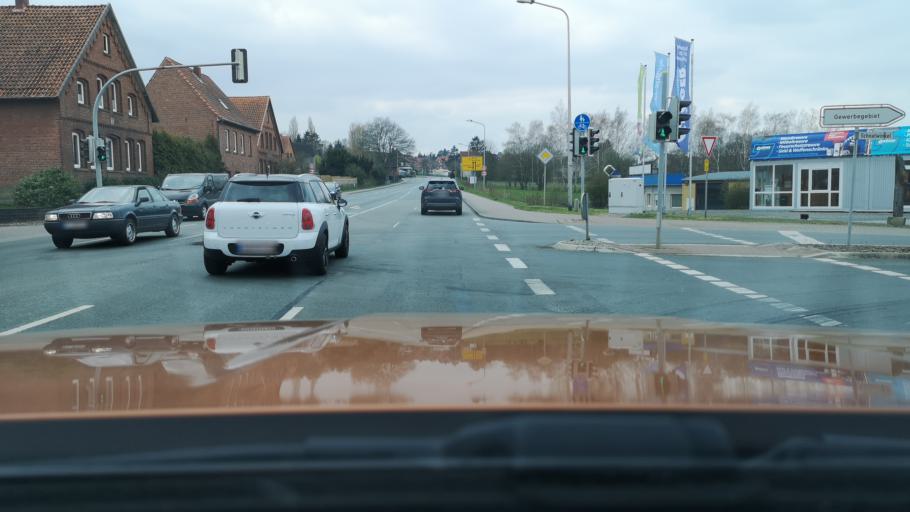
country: DE
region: Lower Saxony
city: Nienstadt
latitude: 52.2952
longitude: 9.1713
